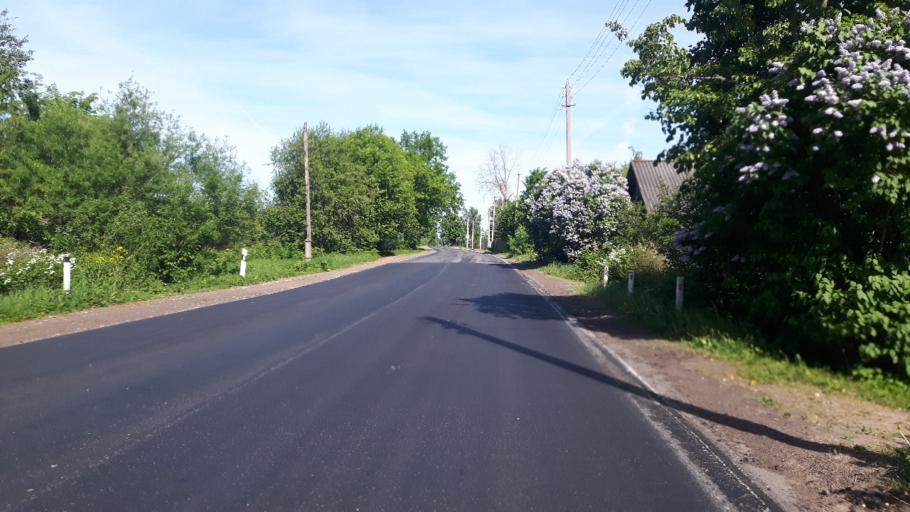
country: RU
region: Leningrad
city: Ivangorod
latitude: 59.4182
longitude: 28.3457
